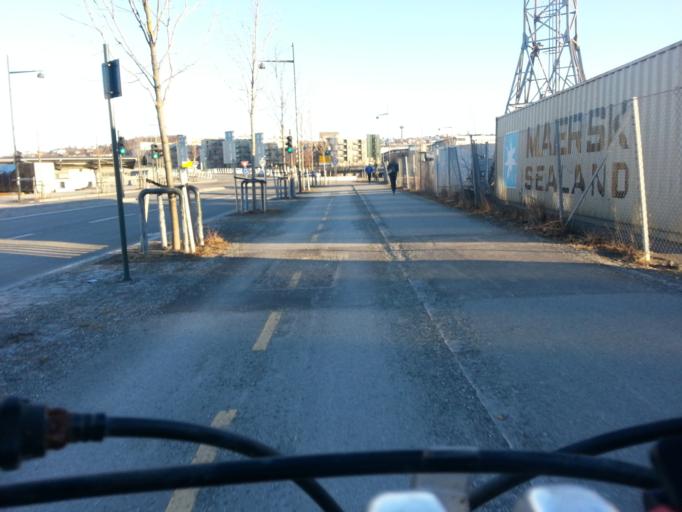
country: NO
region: Sor-Trondelag
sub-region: Trondheim
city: Trondheim
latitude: 63.4389
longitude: 10.4061
